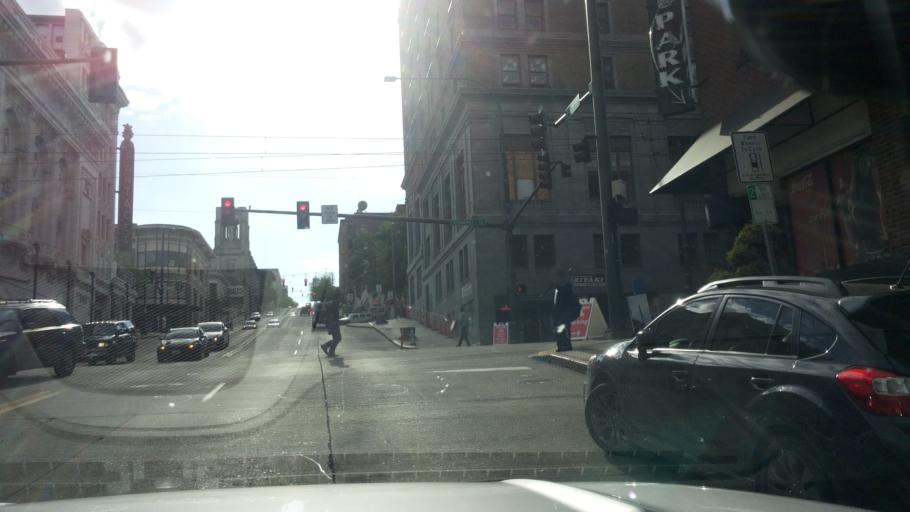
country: US
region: Washington
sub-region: Pierce County
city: Tacoma
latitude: 47.2555
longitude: -122.4392
